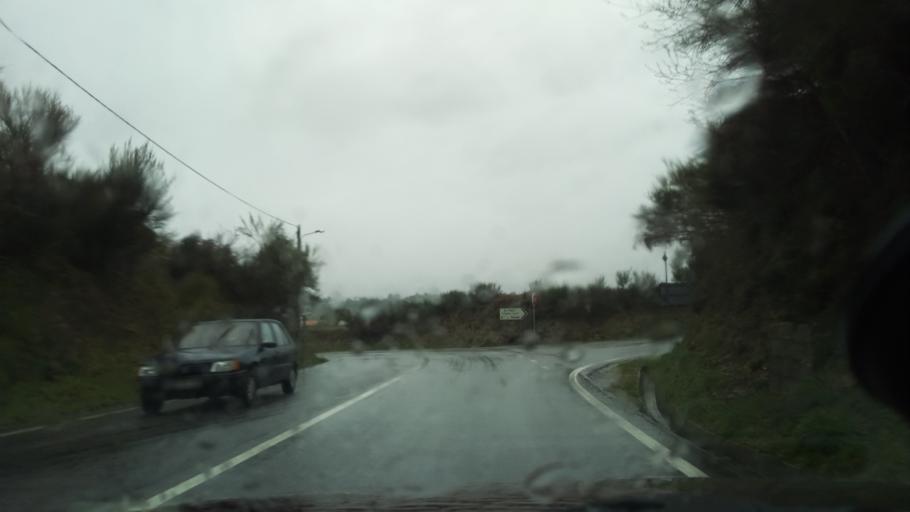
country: PT
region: Guarda
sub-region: Manteigas
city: Manteigas
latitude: 40.5055
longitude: -7.5856
